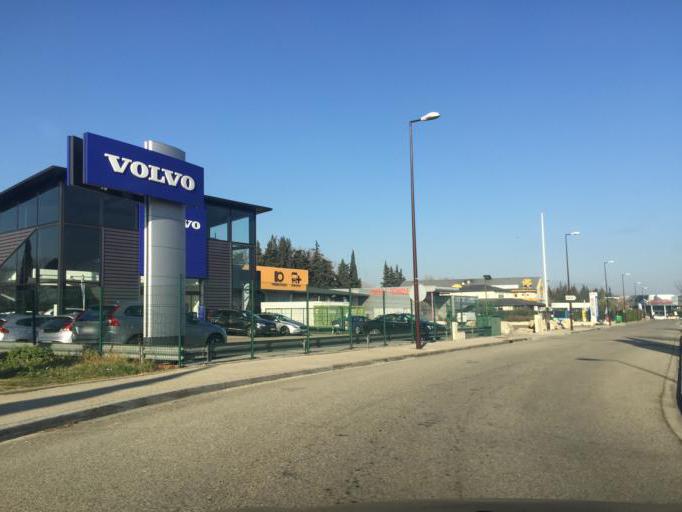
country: FR
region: Provence-Alpes-Cote d'Azur
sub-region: Departement du Vaucluse
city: Montfavet
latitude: 43.9173
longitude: 4.8715
